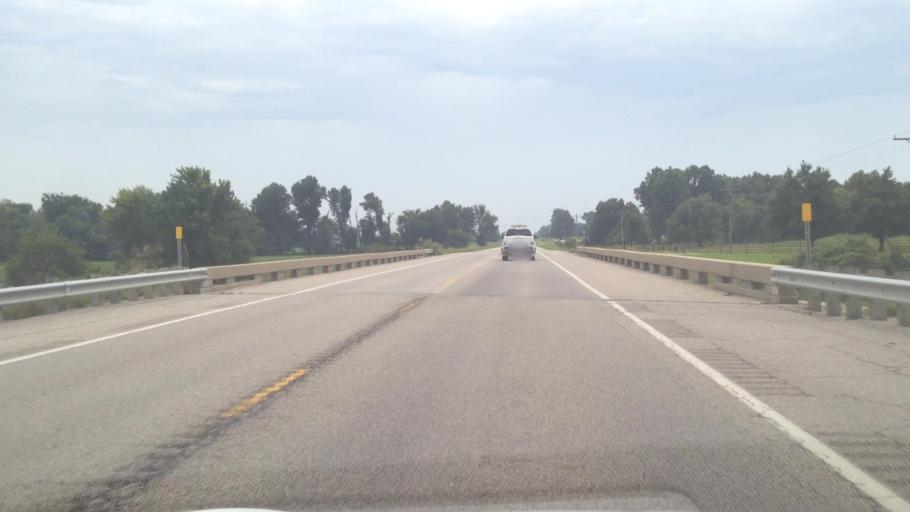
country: US
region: Missouri
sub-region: Jasper County
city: Carl Junction
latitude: 37.2027
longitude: -94.7048
